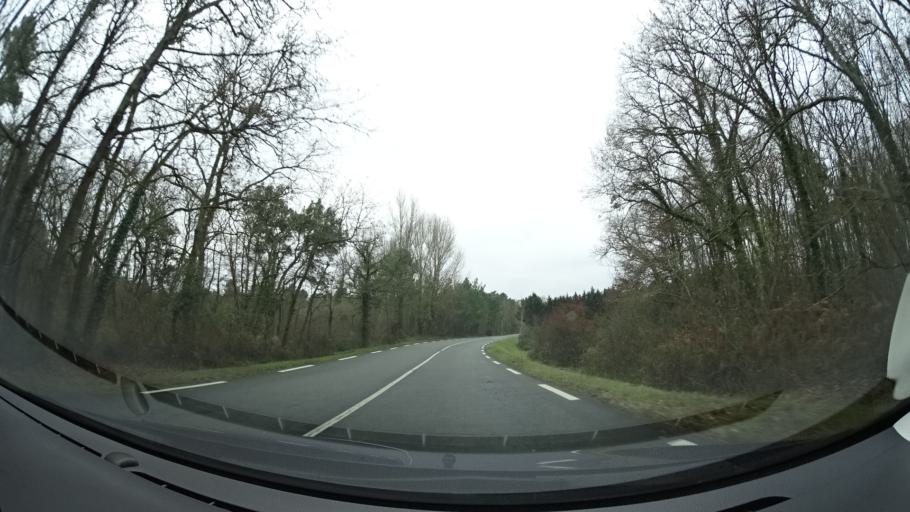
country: FR
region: Aquitaine
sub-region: Departement du Lot-et-Garonne
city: Buzet-sur-Baise
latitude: 44.2377
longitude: 0.2345
